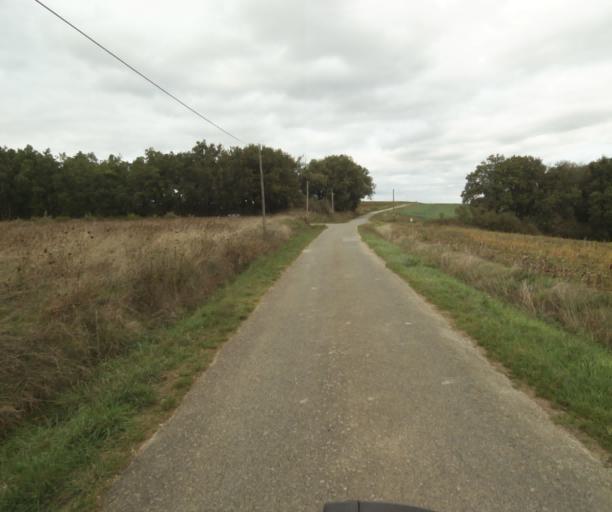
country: FR
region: Midi-Pyrenees
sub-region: Departement du Tarn-et-Garonne
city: Beaumont-de-Lomagne
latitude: 43.8432
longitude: 1.0956
